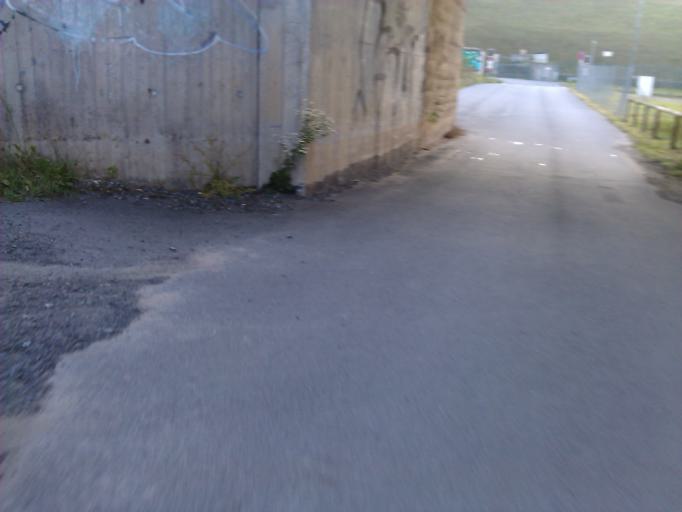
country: DE
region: Hesse
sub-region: Regierungsbezirk Darmstadt
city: Darmstadt
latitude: 49.8962
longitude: 8.6401
